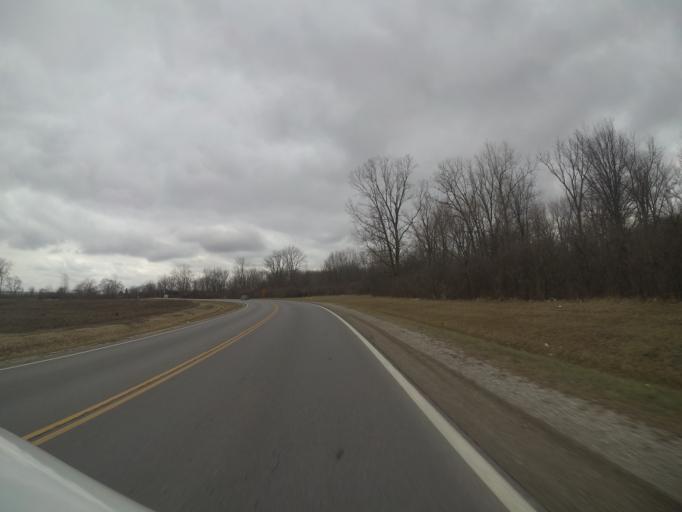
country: US
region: Ohio
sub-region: Wood County
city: Walbridge
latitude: 41.6078
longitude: -83.5176
